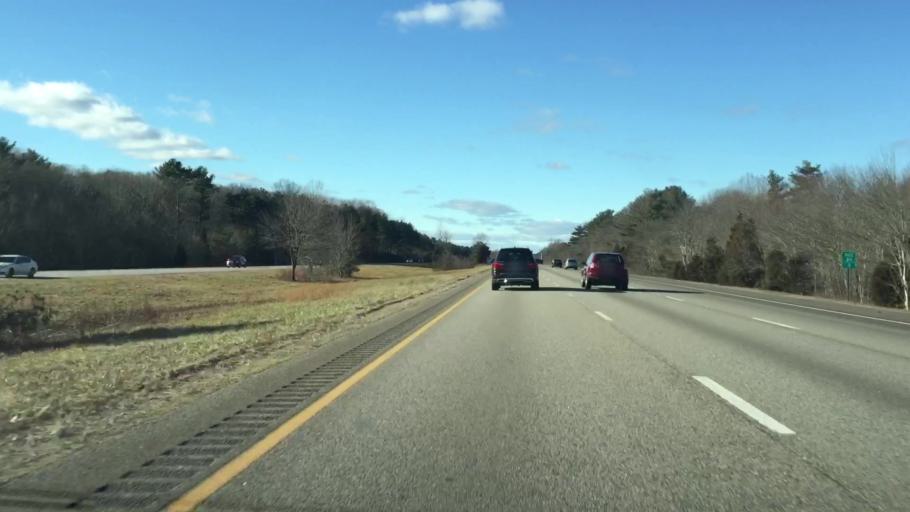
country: US
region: Massachusetts
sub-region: Bristol County
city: Norton Center
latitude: 41.9958
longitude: -71.1903
